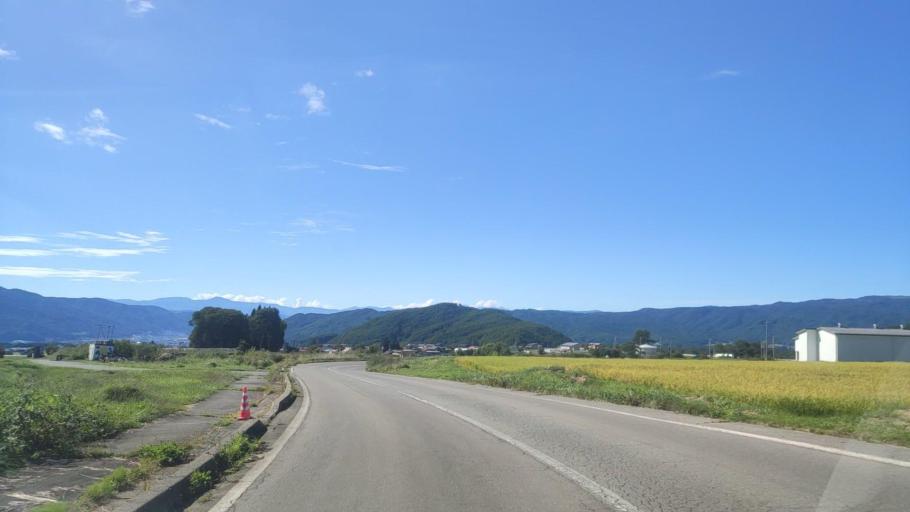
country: JP
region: Nagano
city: Chino
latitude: 35.9884
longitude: 138.2173
